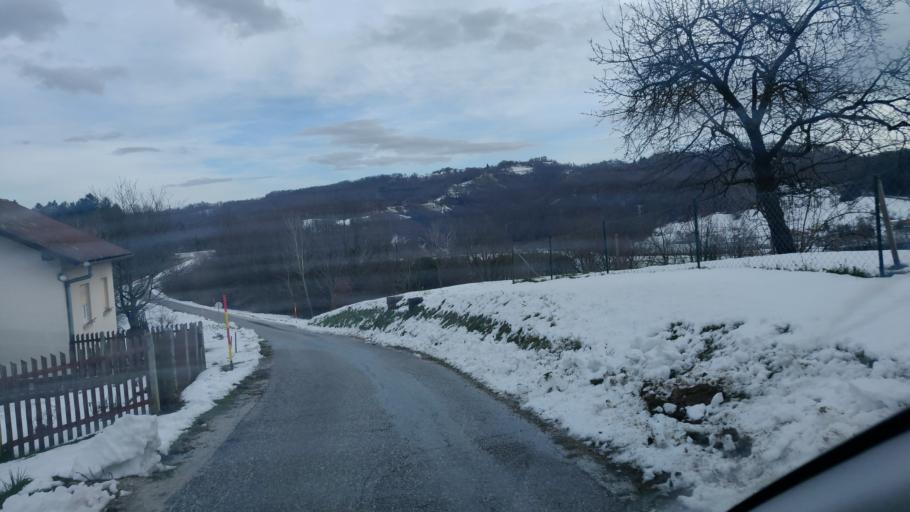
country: SI
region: Makole
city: Makole
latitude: 46.3251
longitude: 15.6640
